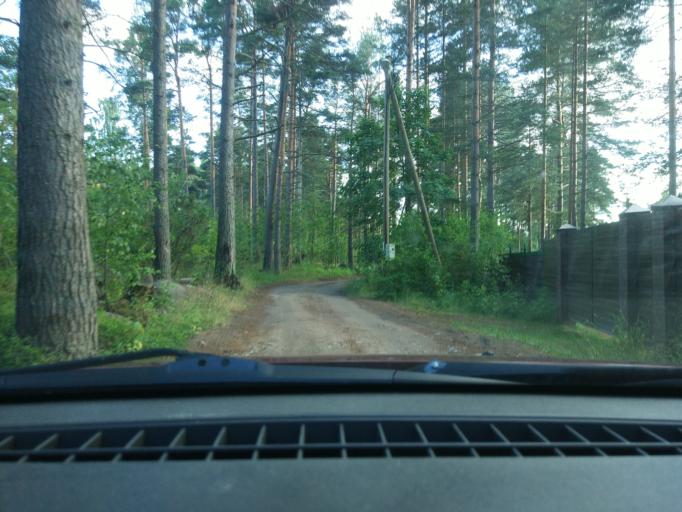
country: RU
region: Leningrad
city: Priozersk
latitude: 60.9409
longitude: 30.0458
